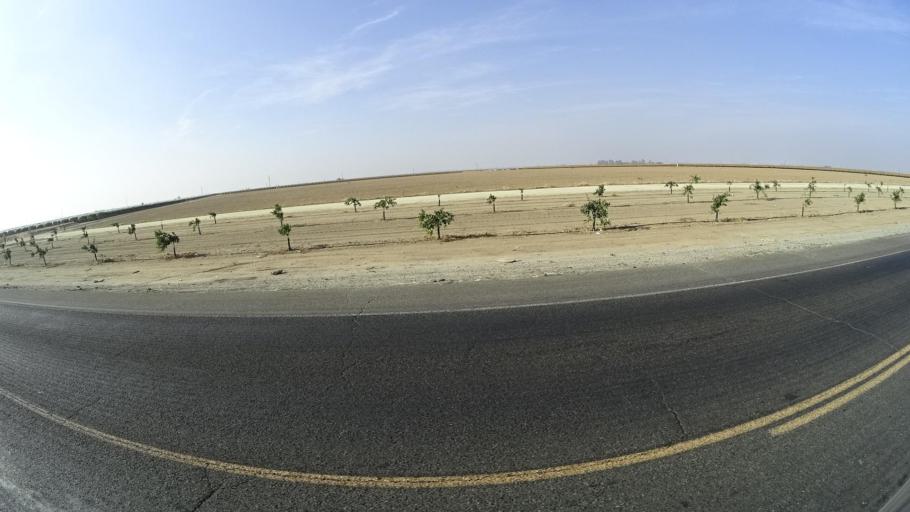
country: US
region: California
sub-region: Tulare County
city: Richgrove
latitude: 35.7256
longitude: -119.1549
